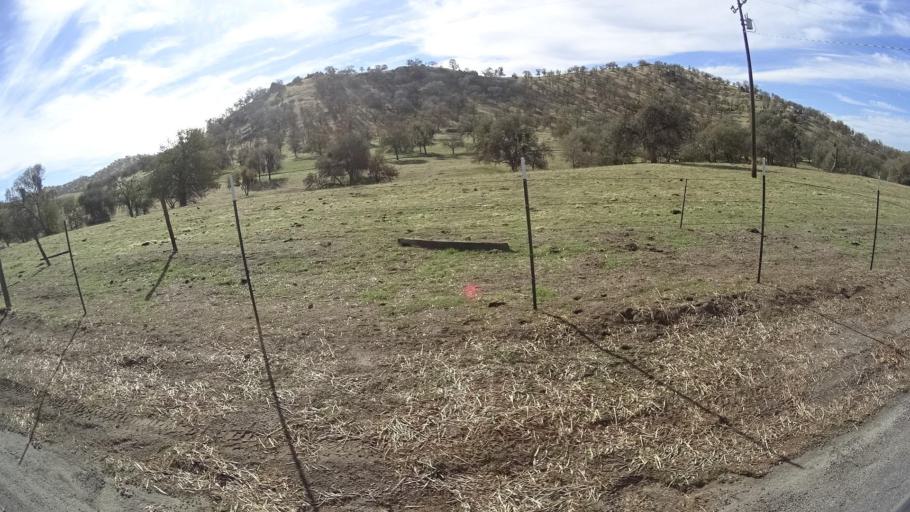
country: US
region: California
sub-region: Kern County
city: Oildale
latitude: 35.5827
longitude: -118.8215
